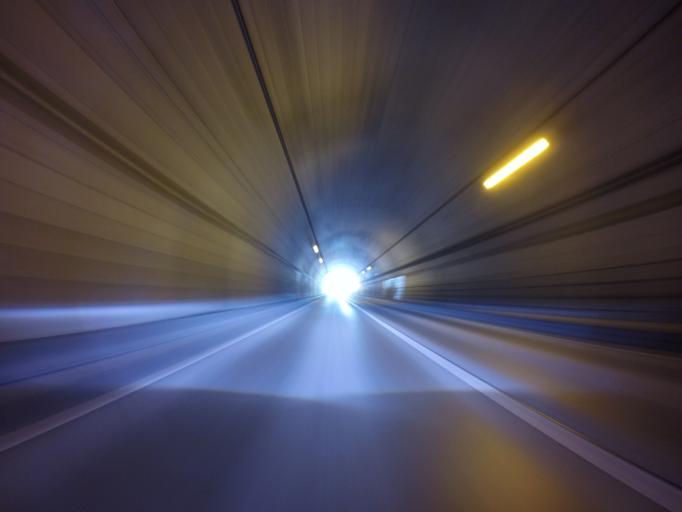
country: JP
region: Shizuoka
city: Shizuoka-shi
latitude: 35.0868
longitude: 138.3761
